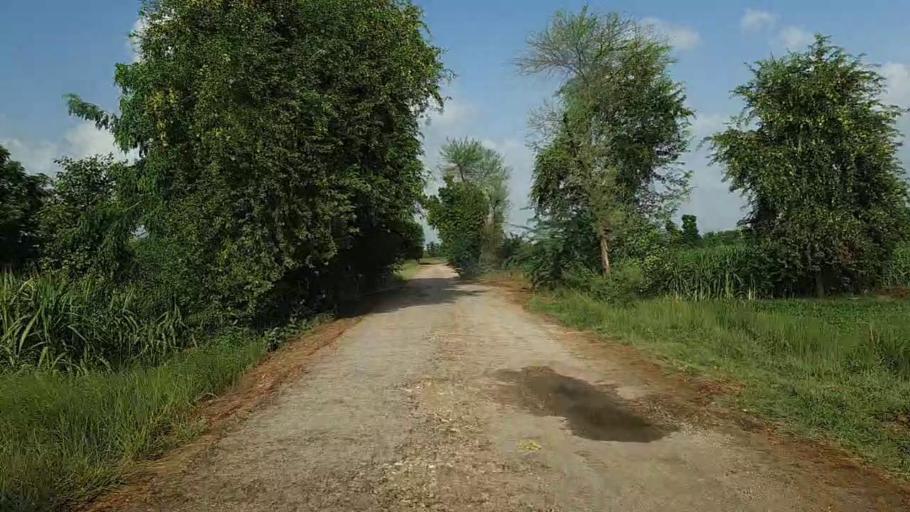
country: PK
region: Sindh
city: Bhiria
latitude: 26.8472
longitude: 68.2360
